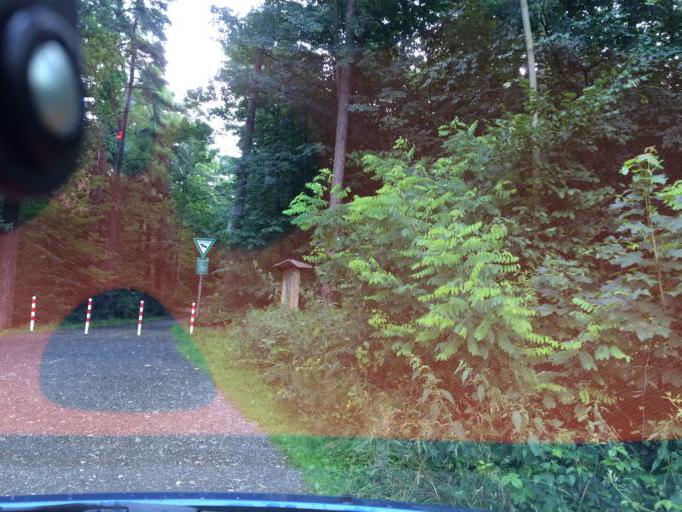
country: DE
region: North Rhine-Westphalia
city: Sankt Augustin
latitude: 50.7342
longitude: 7.1719
